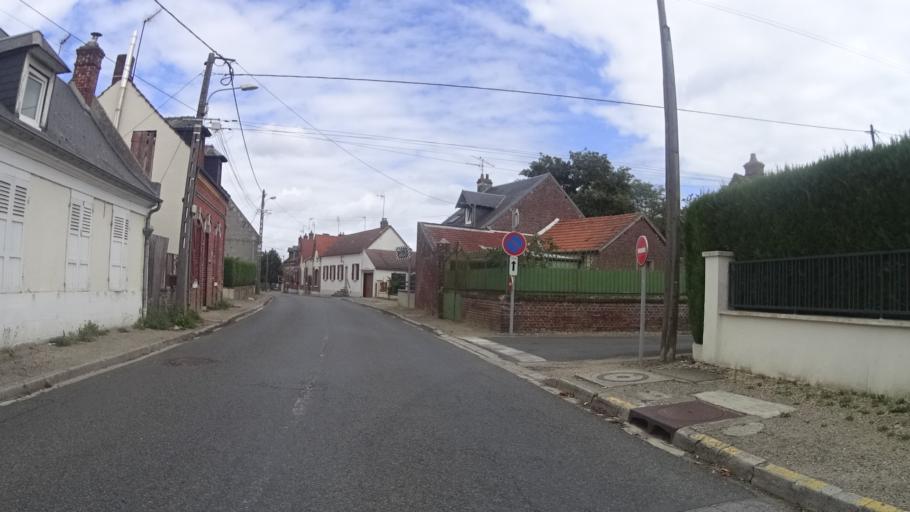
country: FR
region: Picardie
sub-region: Departement de l'Oise
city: Noyon
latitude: 49.5575
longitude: 2.9927
